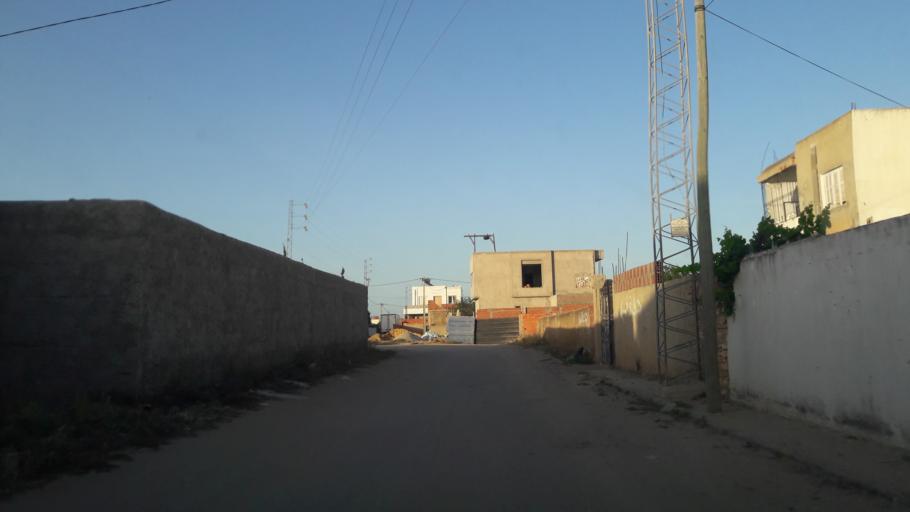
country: TN
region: Safaqis
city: Al Qarmadah
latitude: 34.8196
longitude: 10.7449
